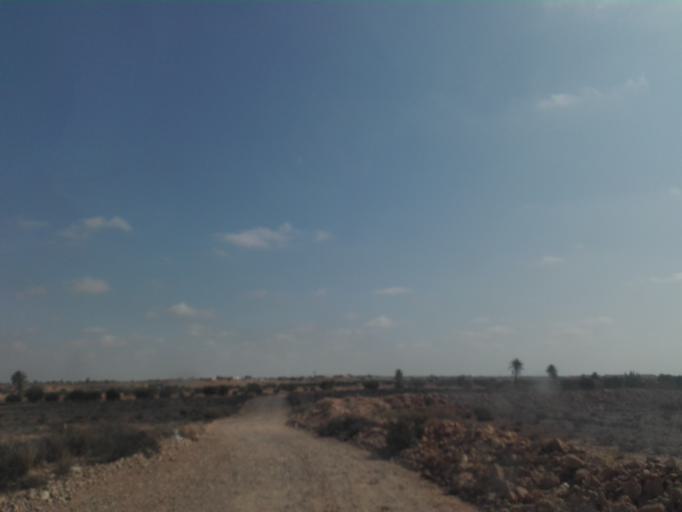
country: TN
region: Madanin
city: Medenine
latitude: 33.4343
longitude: 10.4218
